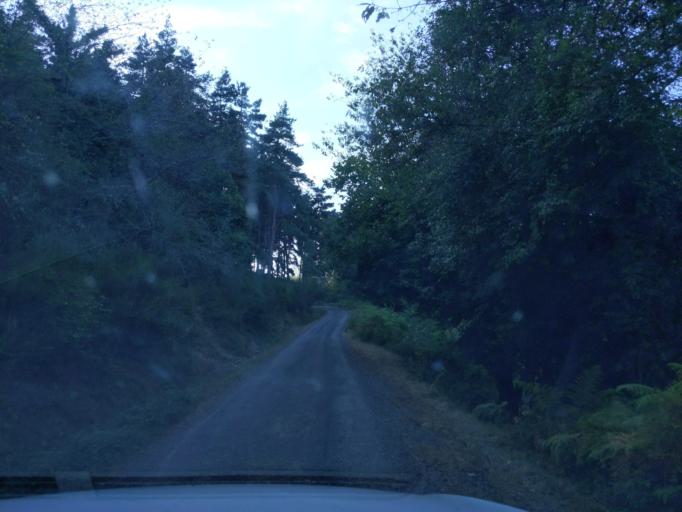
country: ES
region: La Rioja
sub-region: Provincia de La Rioja
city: Ojacastro
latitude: 42.3776
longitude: -3.0119
